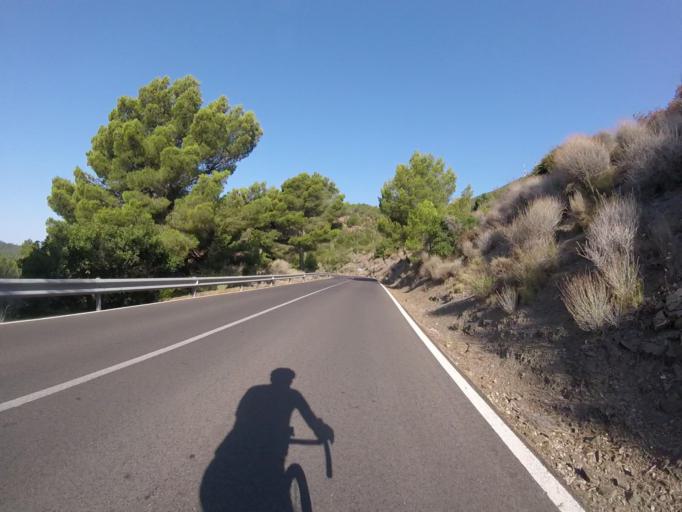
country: ES
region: Valencia
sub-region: Provincia de Castello
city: Benicassim
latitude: 40.0795
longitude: 0.0402
